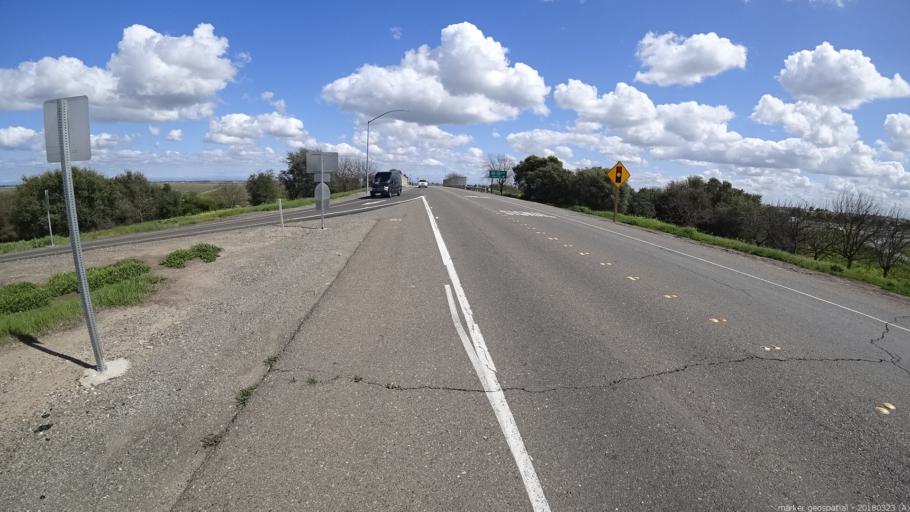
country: US
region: California
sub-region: Sacramento County
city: Elverta
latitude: 38.6855
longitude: -121.5414
